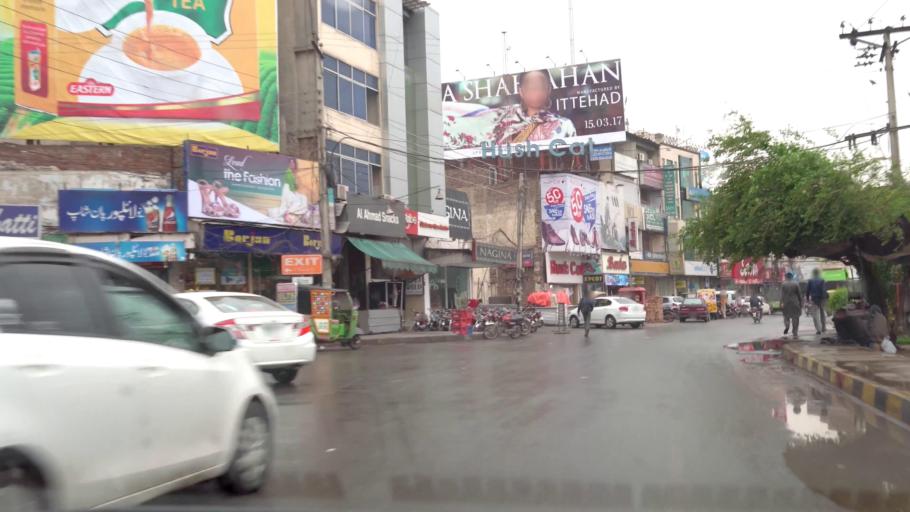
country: PK
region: Punjab
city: Faisalabad
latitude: 31.4116
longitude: 73.1149
